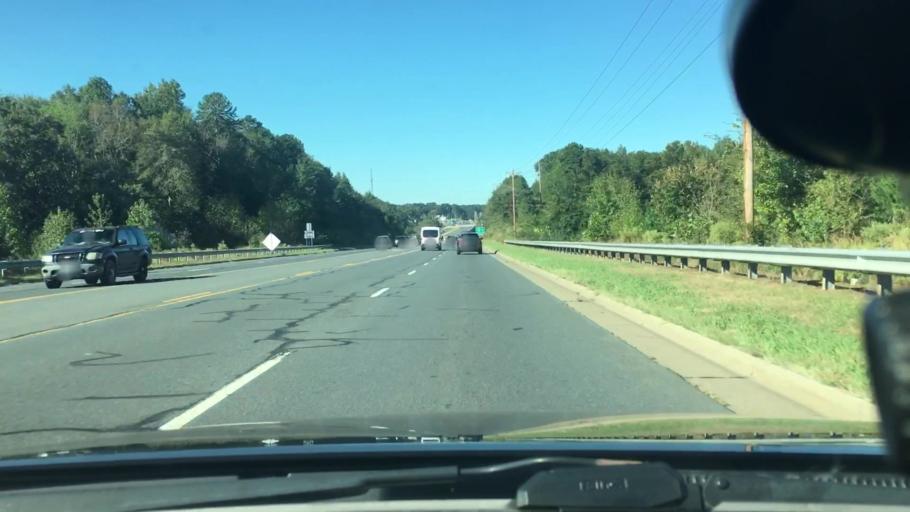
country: US
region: North Carolina
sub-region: Stanly County
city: Albemarle
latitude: 35.3414
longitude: -80.1877
